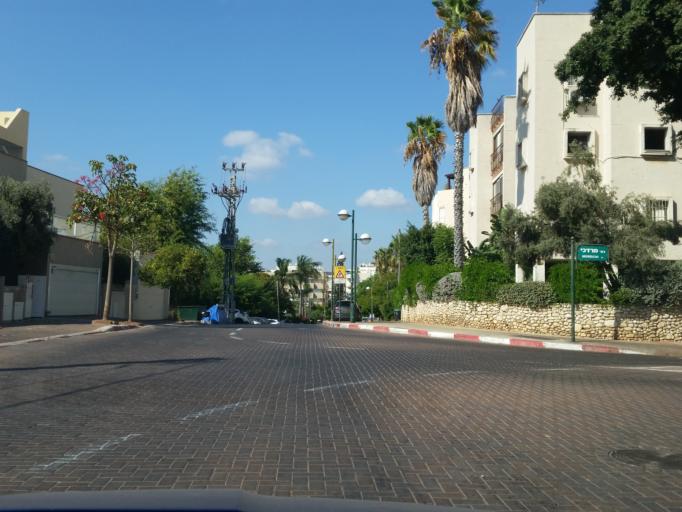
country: IL
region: Tel Aviv
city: Ramat HaSharon
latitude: 32.1385
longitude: 34.8387
